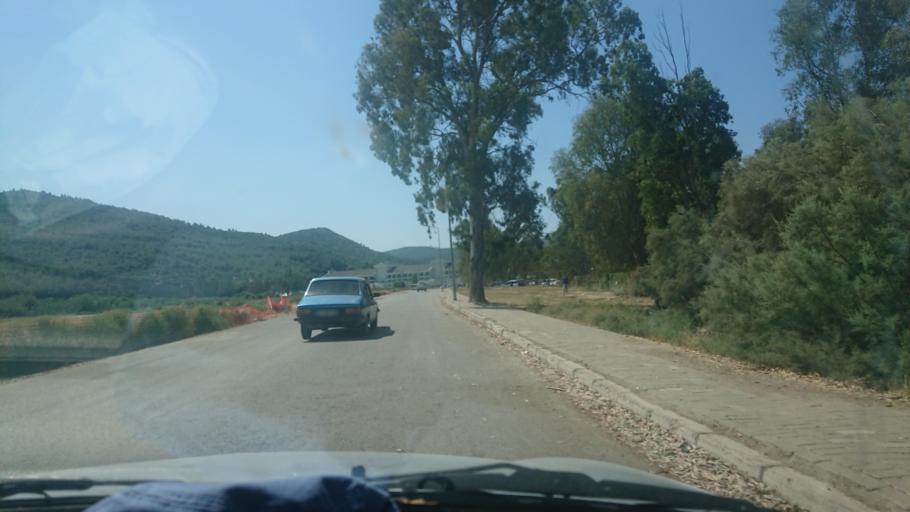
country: TR
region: Aydin
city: Kusadasi
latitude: 37.9397
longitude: 27.2773
